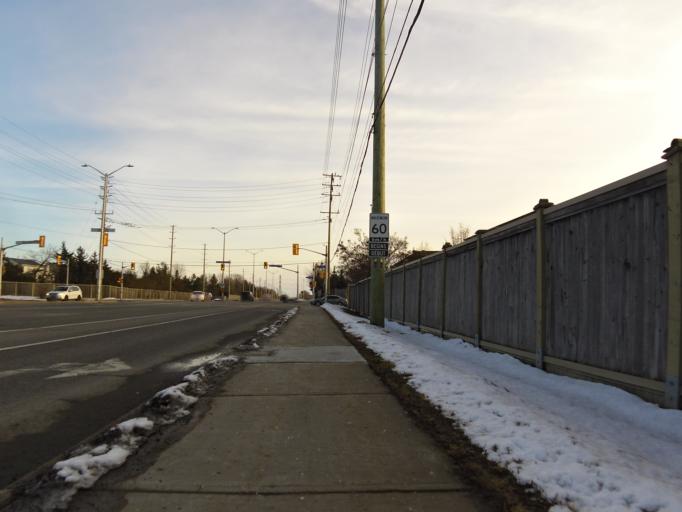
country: CA
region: Ontario
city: Bells Corners
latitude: 45.2905
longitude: -75.8925
